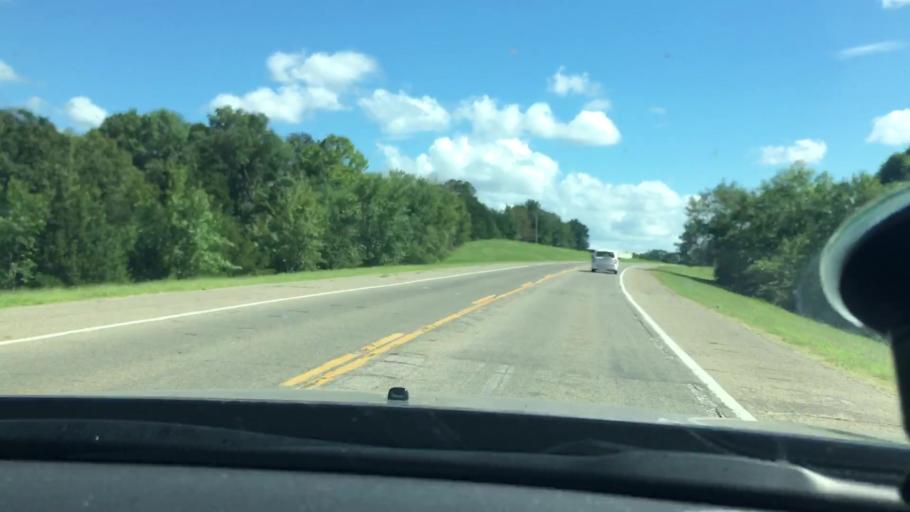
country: US
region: Oklahoma
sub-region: Sequoyah County
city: Vian
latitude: 35.5152
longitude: -94.9708
